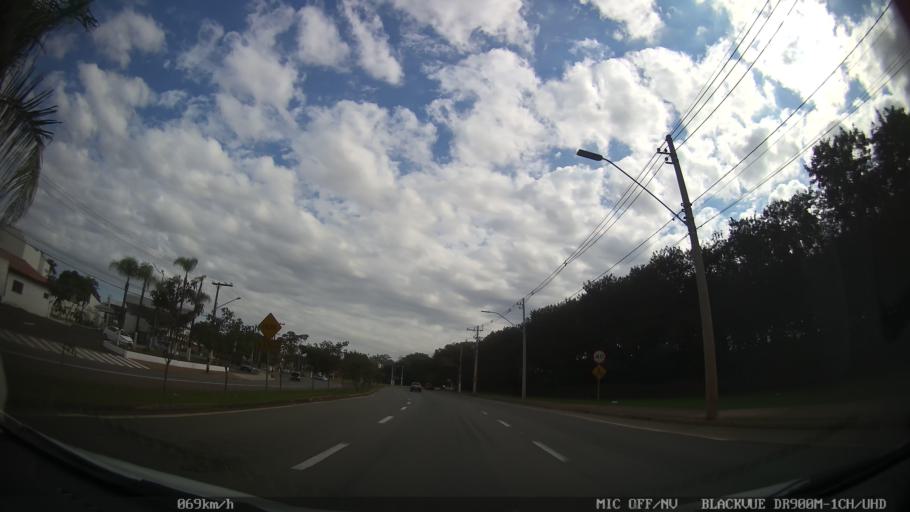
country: BR
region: Sao Paulo
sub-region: Limeira
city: Limeira
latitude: -22.5450
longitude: -47.4209
